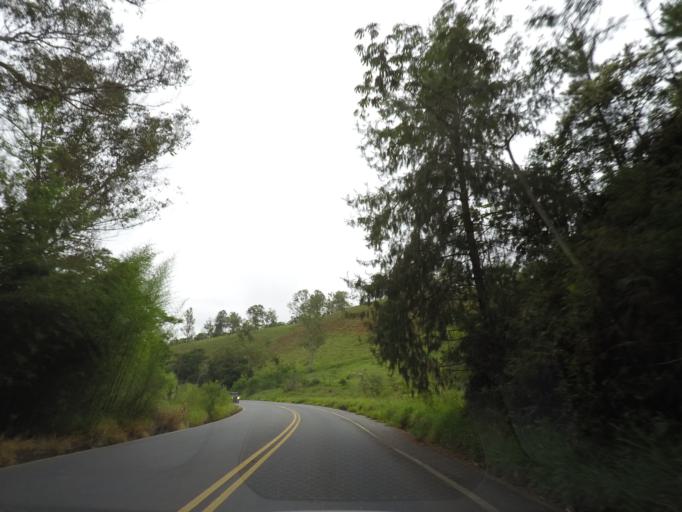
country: BR
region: Sao Paulo
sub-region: Cunha
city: Cunha
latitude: -22.9439
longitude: -45.0617
